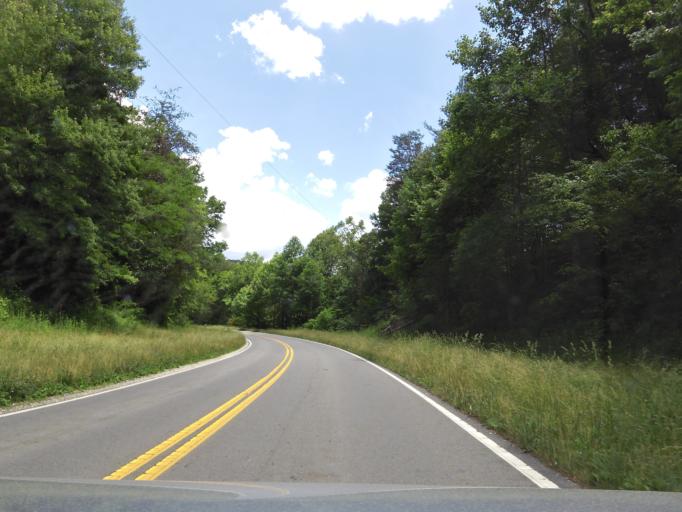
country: US
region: North Carolina
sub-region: Graham County
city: Robbinsville
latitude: 35.3684
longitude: -83.8419
